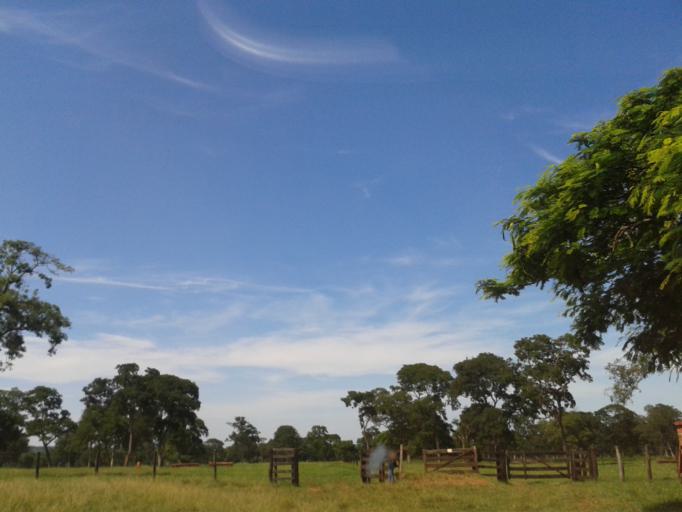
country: BR
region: Minas Gerais
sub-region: Santa Vitoria
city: Santa Vitoria
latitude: -19.1600
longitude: -50.5054
